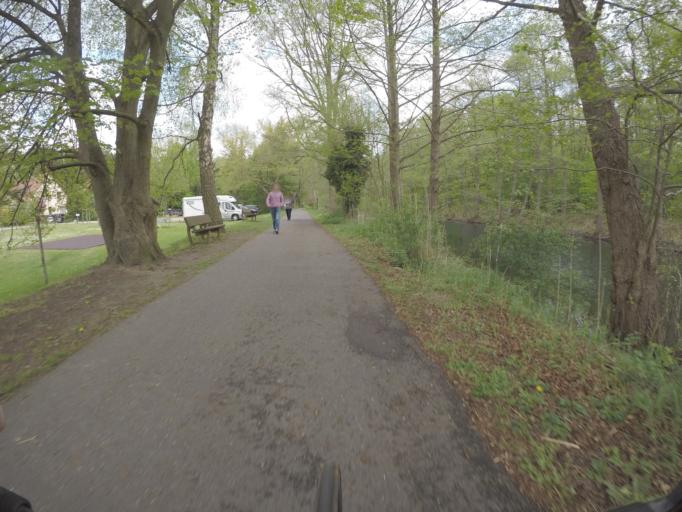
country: DE
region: Brandenburg
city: Marienwerder
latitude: 52.8952
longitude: 13.6425
